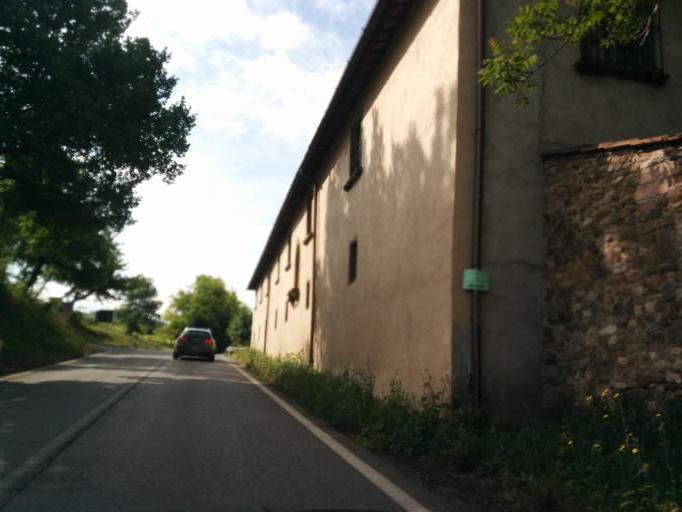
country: IT
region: Tuscany
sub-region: Province of Florence
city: San Casciano in Val di Pesa
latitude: 43.6251
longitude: 11.1848
